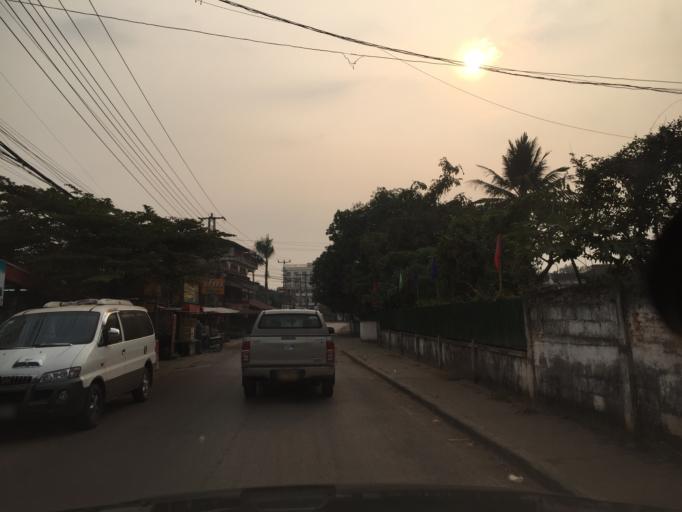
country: LA
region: Vientiane
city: Vientiane
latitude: 17.9745
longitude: 102.6120
